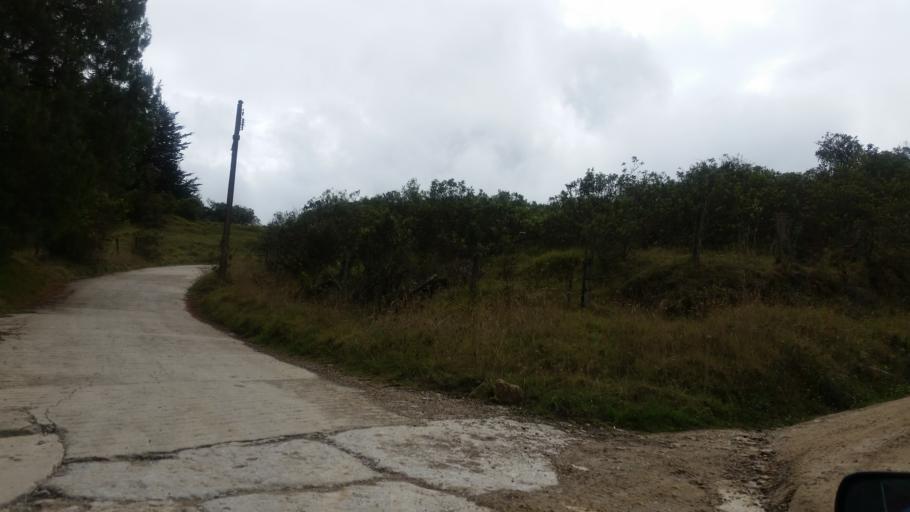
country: CO
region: Cundinamarca
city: La Calera
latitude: 4.7149
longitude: -73.9466
